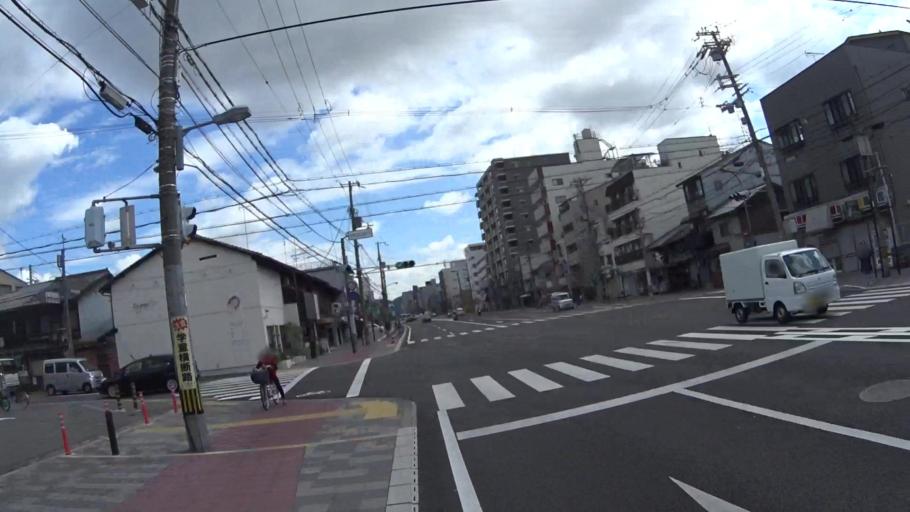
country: JP
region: Kyoto
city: Kyoto
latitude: 34.9893
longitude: 135.7457
